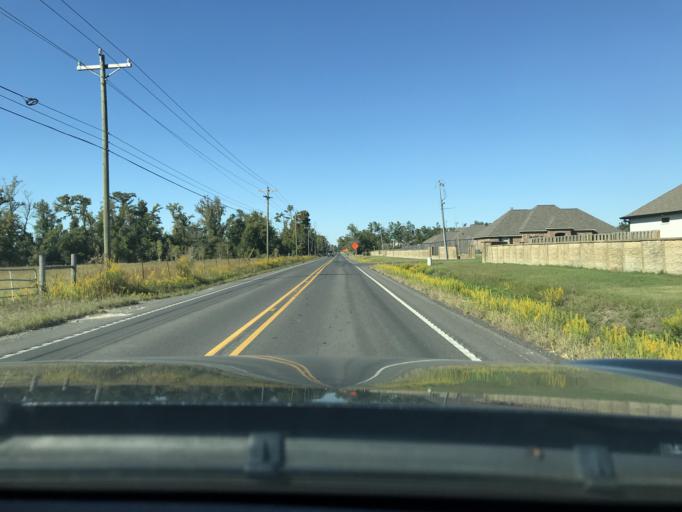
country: US
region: Louisiana
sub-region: Calcasieu Parish
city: Westlake
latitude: 30.3096
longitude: -93.2583
